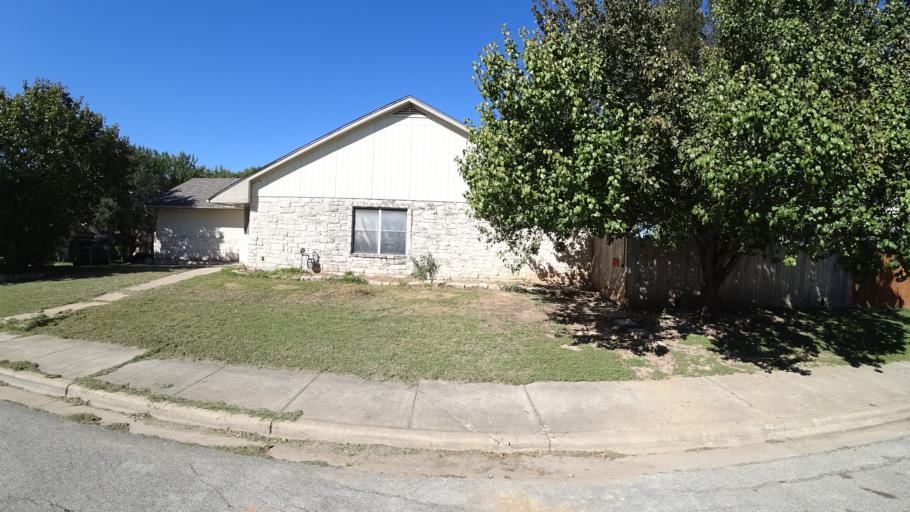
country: US
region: Texas
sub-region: Travis County
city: Manor
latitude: 30.3325
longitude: -97.6471
